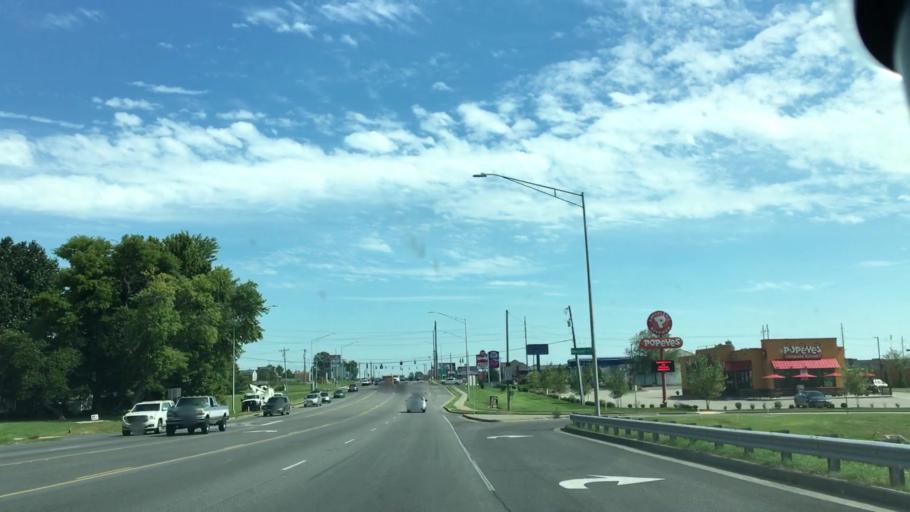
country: US
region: Kentucky
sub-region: Daviess County
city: Owensboro
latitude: 37.7571
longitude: -87.0696
